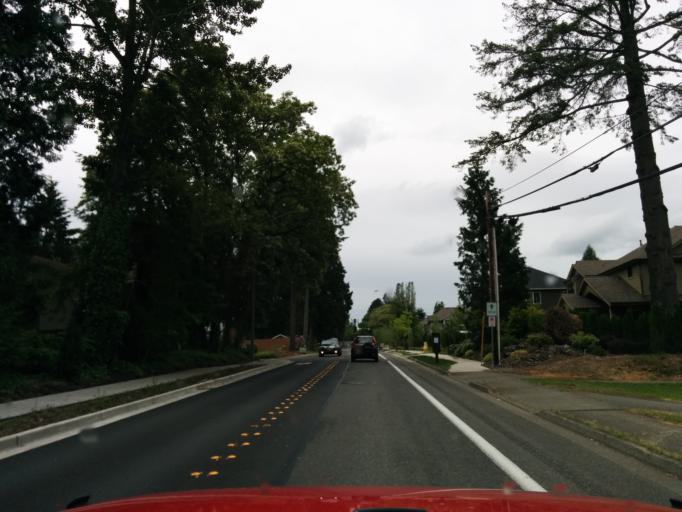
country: US
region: Washington
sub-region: King County
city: Redmond
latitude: 47.6546
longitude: -122.1291
